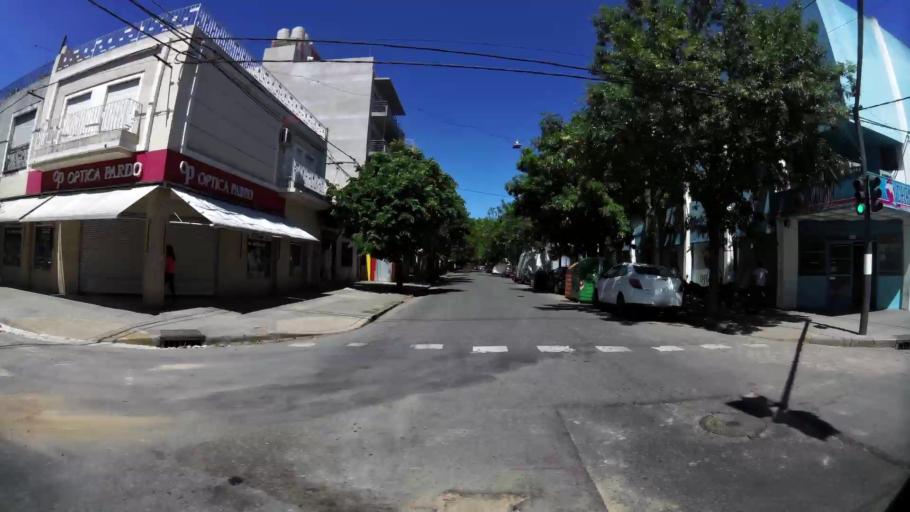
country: AR
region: Santa Fe
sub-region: Departamento de Rosario
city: Rosario
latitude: -32.9360
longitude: -60.6697
